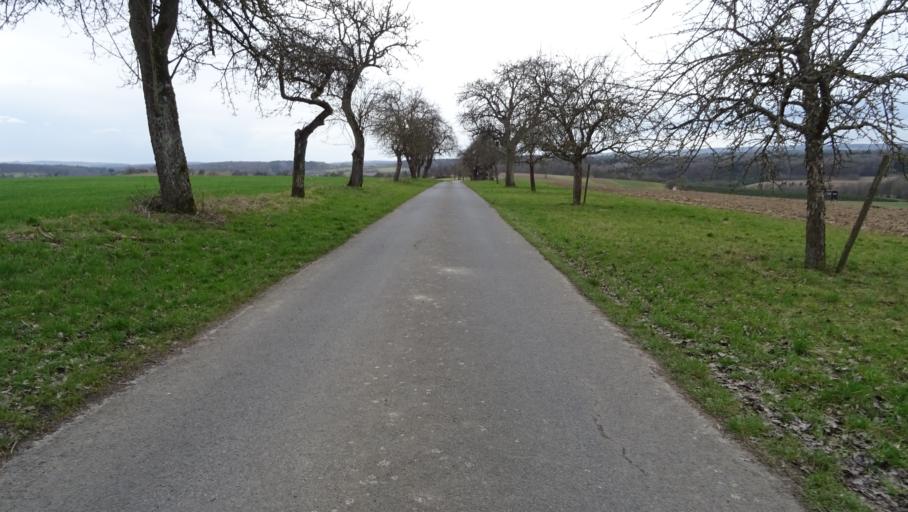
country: DE
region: Baden-Wuerttemberg
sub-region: Karlsruhe Region
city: Limbach
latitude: 49.4339
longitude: 9.2584
